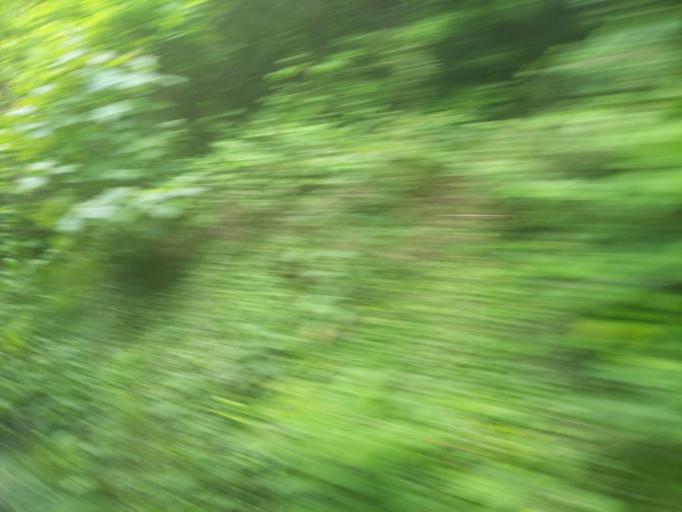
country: GB
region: England
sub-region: Devon
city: Winkleigh
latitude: 50.9269
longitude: -3.9021
